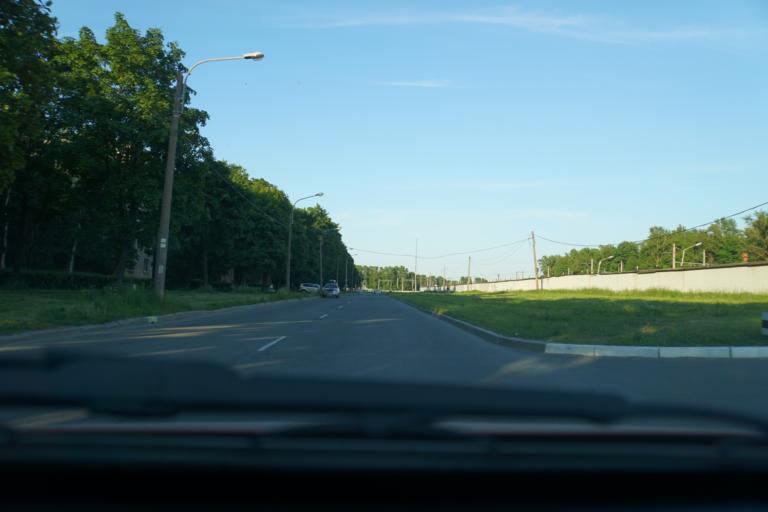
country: RU
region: St.-Petersburg
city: Avtovo
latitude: 59.8647
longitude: 30.2801
